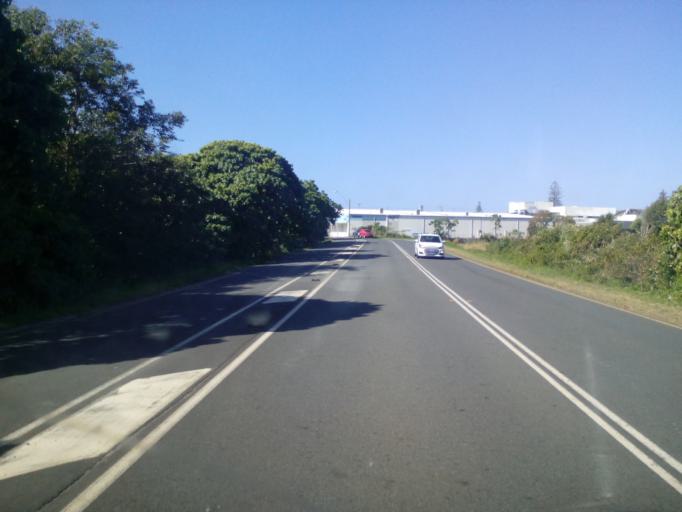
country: AU
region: New South Wales
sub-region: Tweed
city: Kingscliff
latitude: -28.2569
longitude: 153.5725
